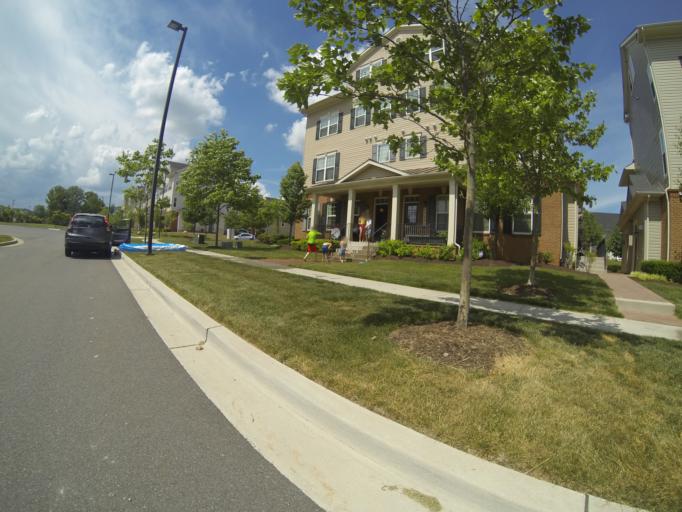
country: US
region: Maryland
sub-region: Montgomery County
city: Clarksburg
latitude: 39.2352
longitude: -77.2782
